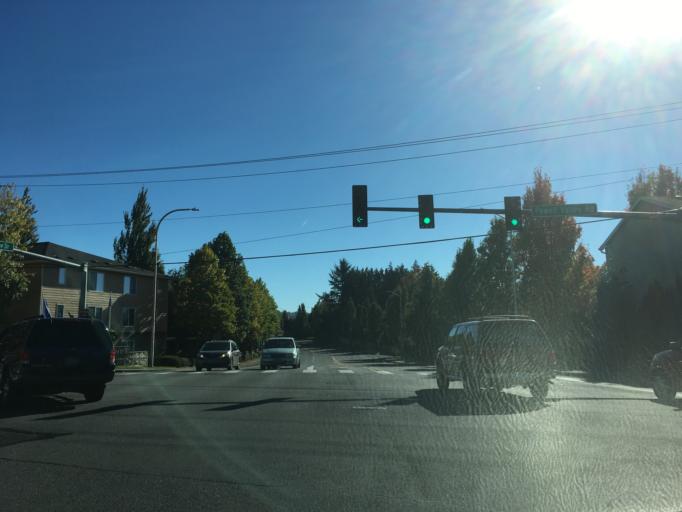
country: US
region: Oregon
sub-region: Multnomah County
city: Gresham
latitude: 45.4920
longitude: -122.3990
